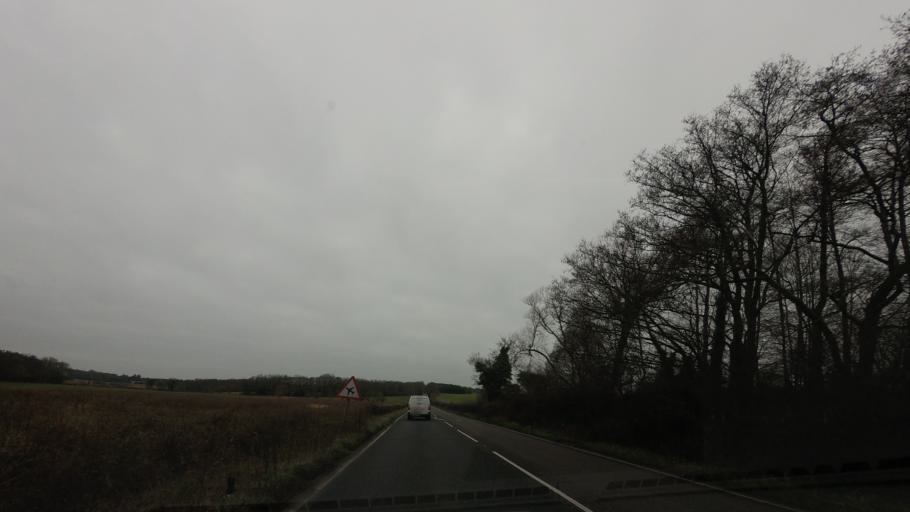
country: GB
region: England
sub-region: East Sussex
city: Battle
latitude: 50.9311
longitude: 0.5244
